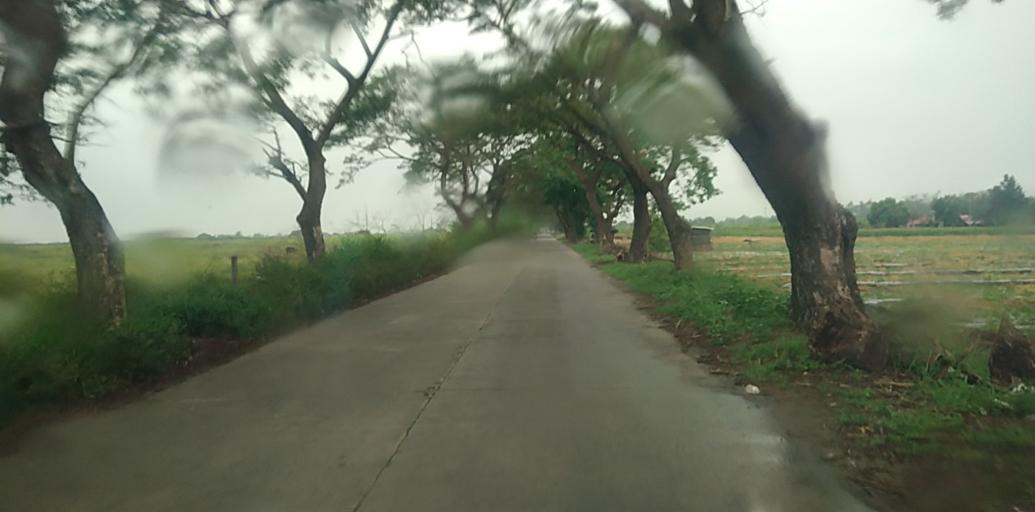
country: PH
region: Central Luzon
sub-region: Province of Pampanga
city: Anao
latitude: 15.1500
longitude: 120.7010
